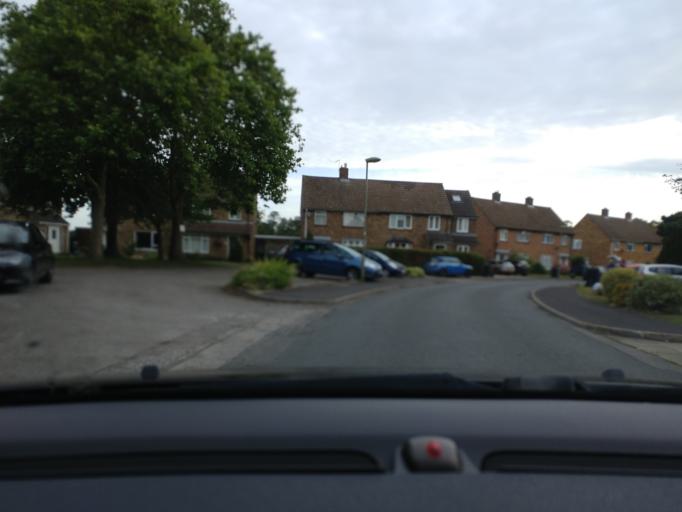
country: GB
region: England
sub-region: Oxfordshire
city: Wallingford
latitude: 51.6075
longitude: -1.1273
